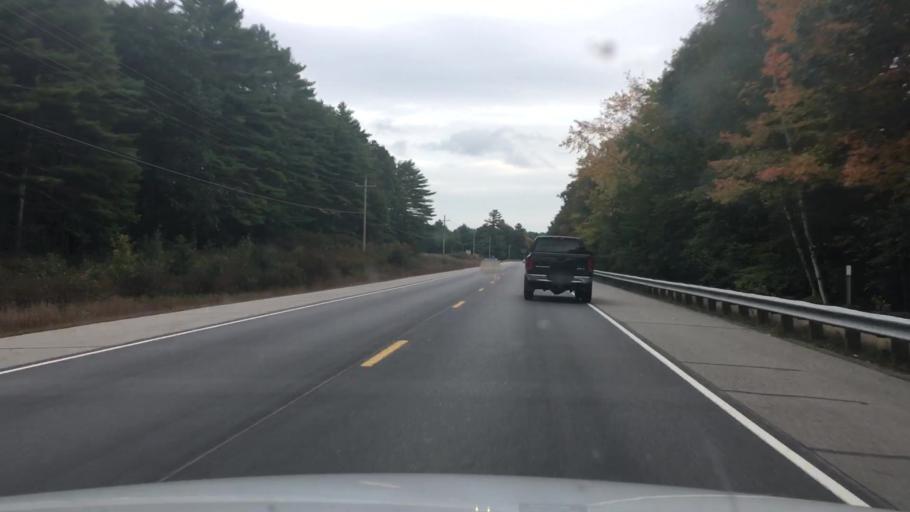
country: US
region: New Hampshire
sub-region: Strafford County
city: New Durham
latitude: 43.4346
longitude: -71.1790
